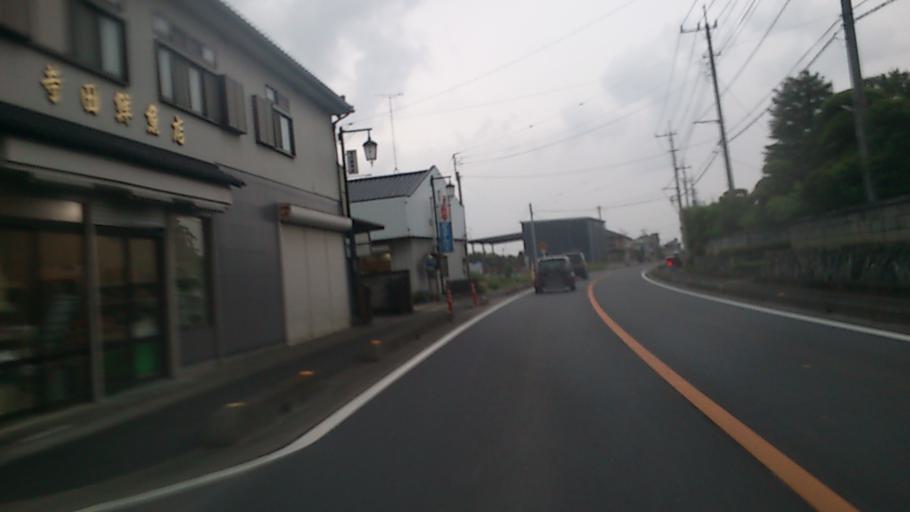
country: JP
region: Saitama
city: Kazo
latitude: 36.1554
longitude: 139.6182
